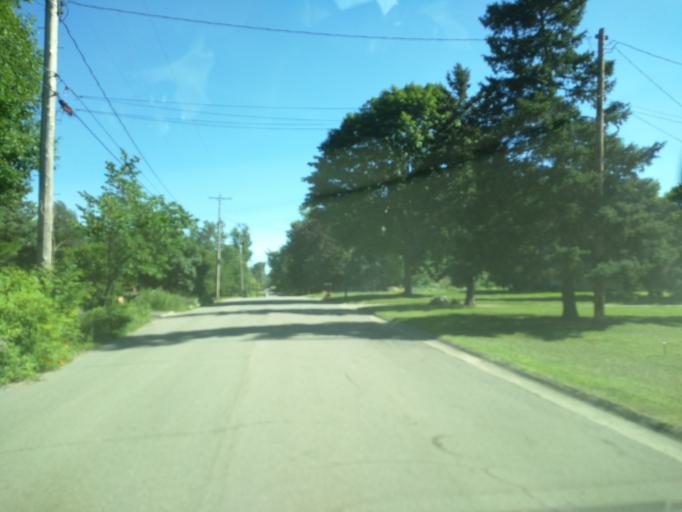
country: US
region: Michigan
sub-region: Eaton County
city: Waverly
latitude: 42.7480
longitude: -84.6361
